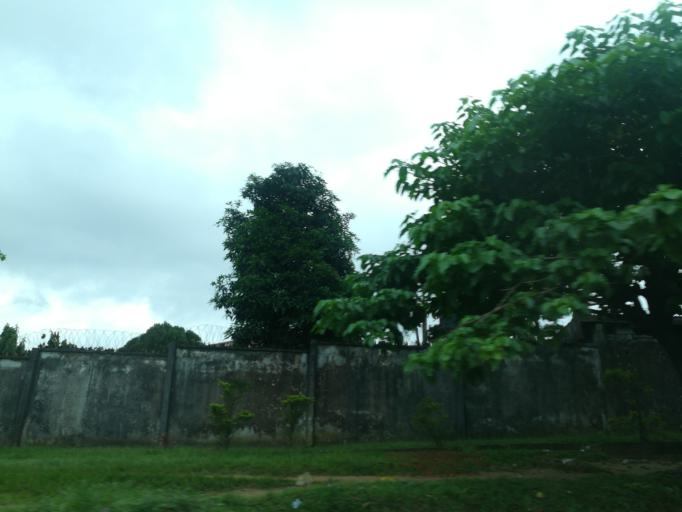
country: NG
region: Rivers
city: Port Harcourt
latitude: 4.8403
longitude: 7.0308
